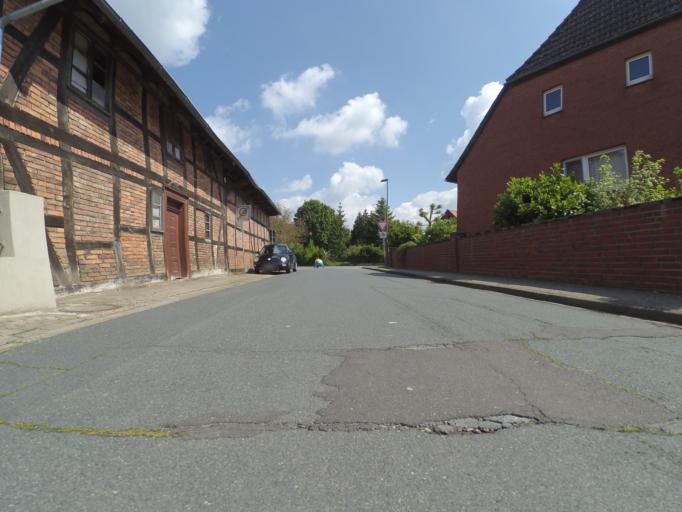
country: DE
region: Lower Saxony
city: Vechelde
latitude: 52.3059
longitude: 10.3153
